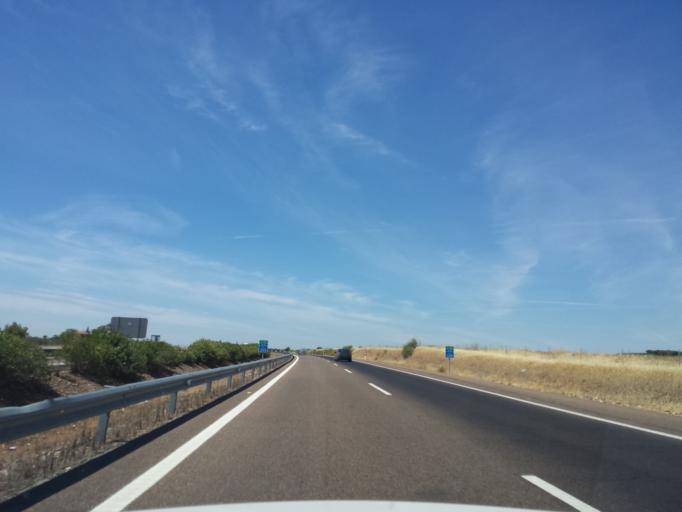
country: ES
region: Extremadura
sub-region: Provincia de Badajoz
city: Trujillanos
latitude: 38.9462
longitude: -6.2934
